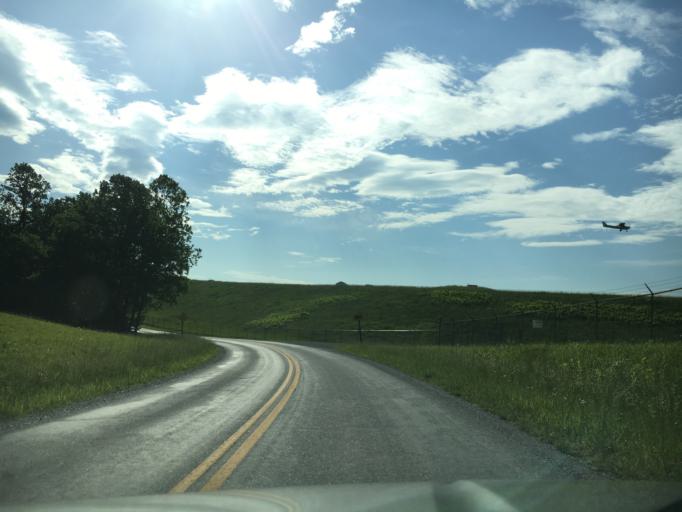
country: US
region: Virginia
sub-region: Campbell County
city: Timberlake
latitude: 37.3348
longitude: -79.1972
